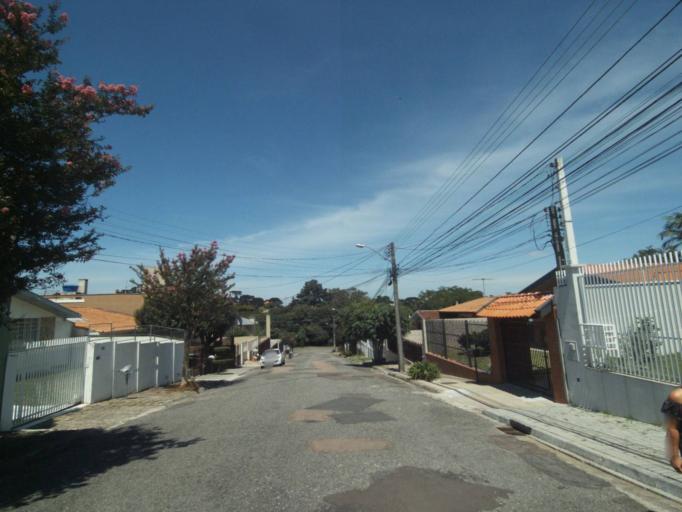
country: BR
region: Parana
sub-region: Curitiba
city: Curitiba
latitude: -25.4643
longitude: -49.2407
